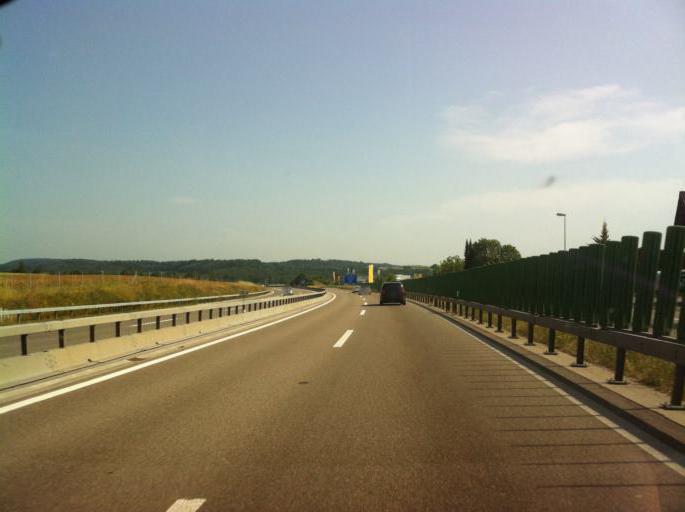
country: CH
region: Zurich
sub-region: Bezirk Andelfingen
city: Kleinandelfingen
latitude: 47.6070
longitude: 8.6871
